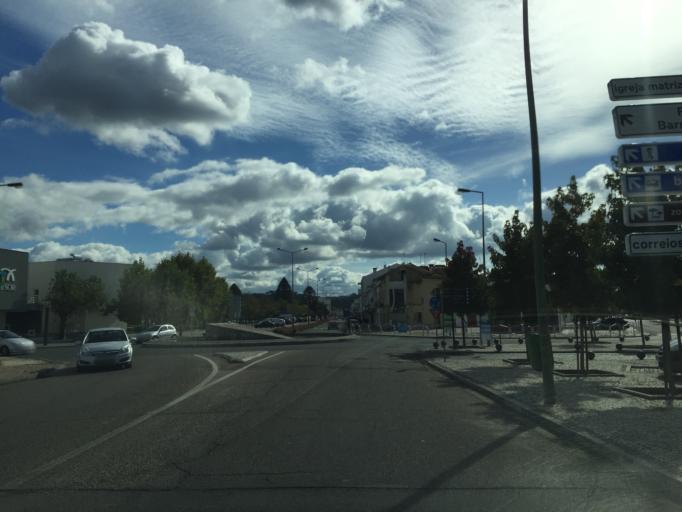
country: PT
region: Portalegre
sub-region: Ponte de Sor
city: Ponte de Sor
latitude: 39.2528
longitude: -8.0097
